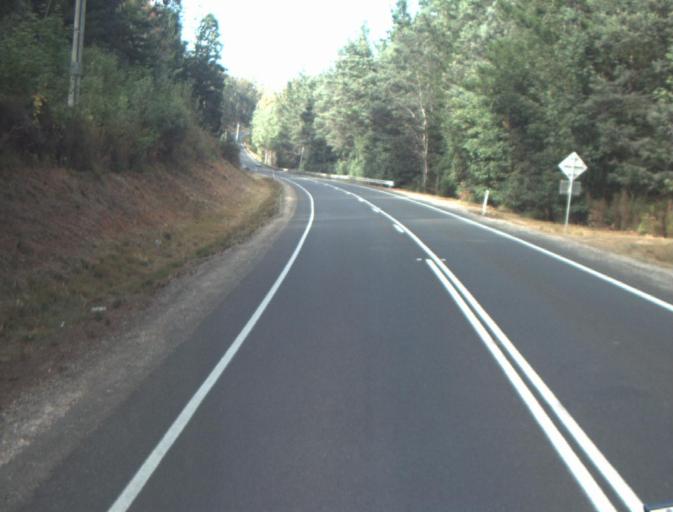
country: AU
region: Tasmania
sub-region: Launceston
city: Mayfield
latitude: -41.3021
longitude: 147.2056
